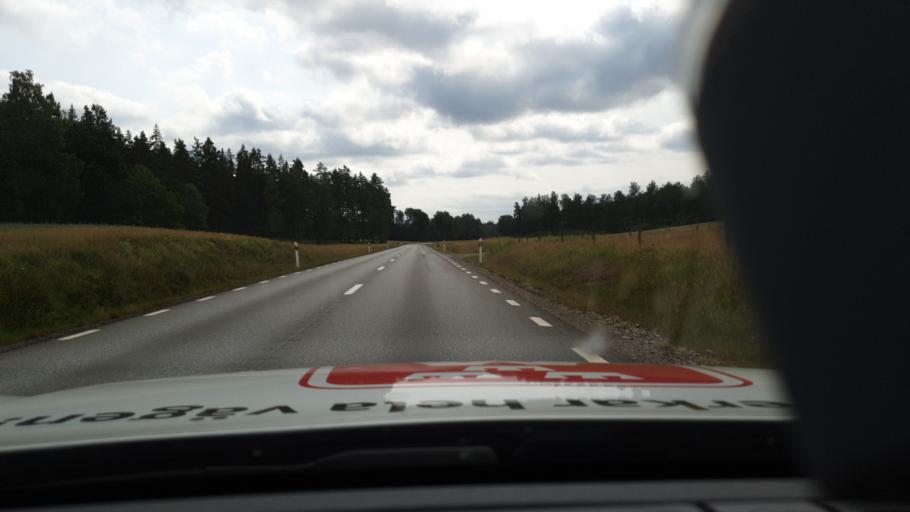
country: SE
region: Joenkoeping
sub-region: Mullsjo Kommun
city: Mullsjoe
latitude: 57.8449
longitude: 13.8543
